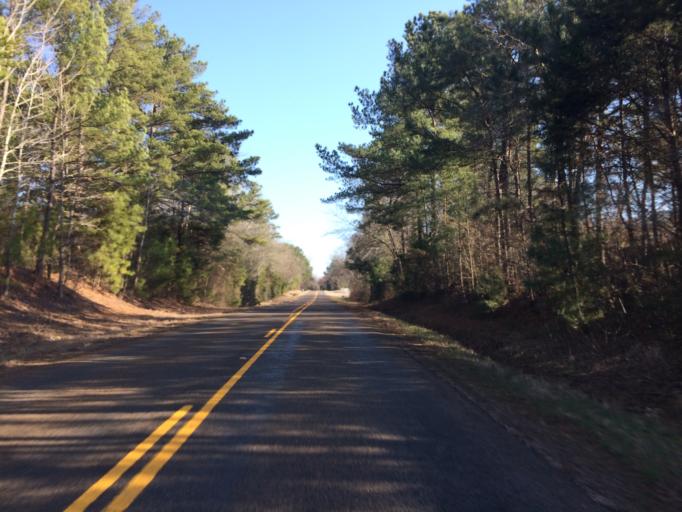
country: US
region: Texas
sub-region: Wood County
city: Quitman
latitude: 32.7071
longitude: -95.3582
